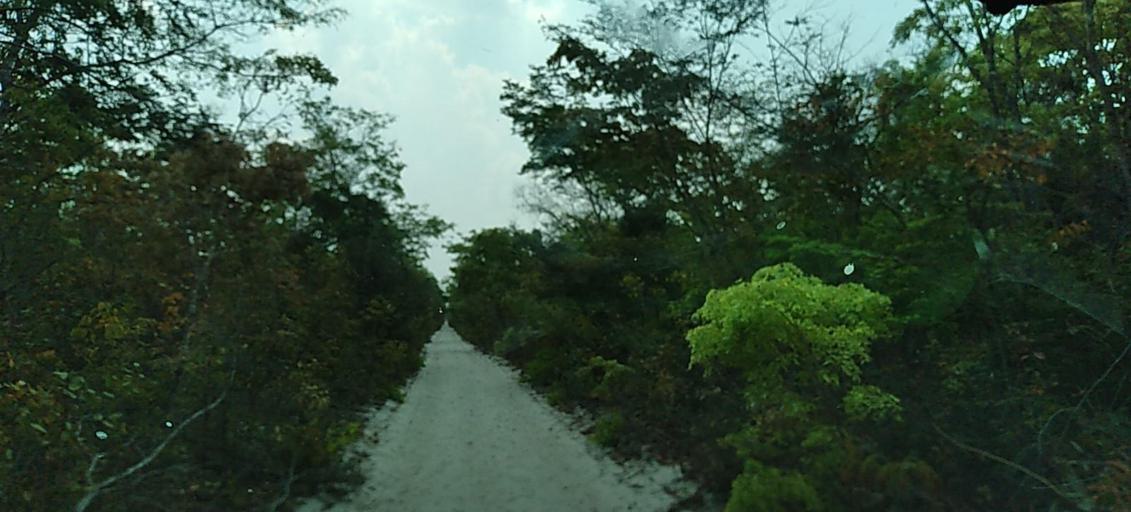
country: ZM
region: North-Western
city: Kabompo
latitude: -13.3993
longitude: 23.8082
